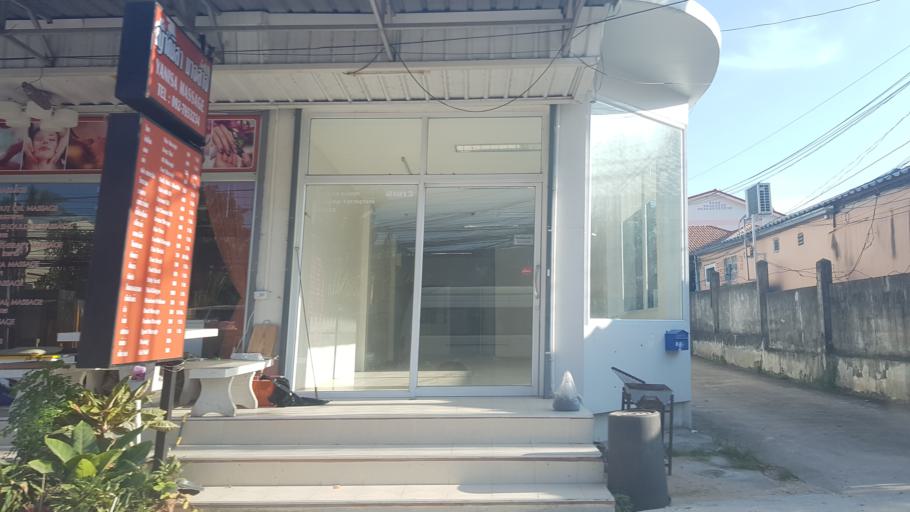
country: TH
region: Surat Thani
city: Ko Samui
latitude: 9.5579
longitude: 100.0561
